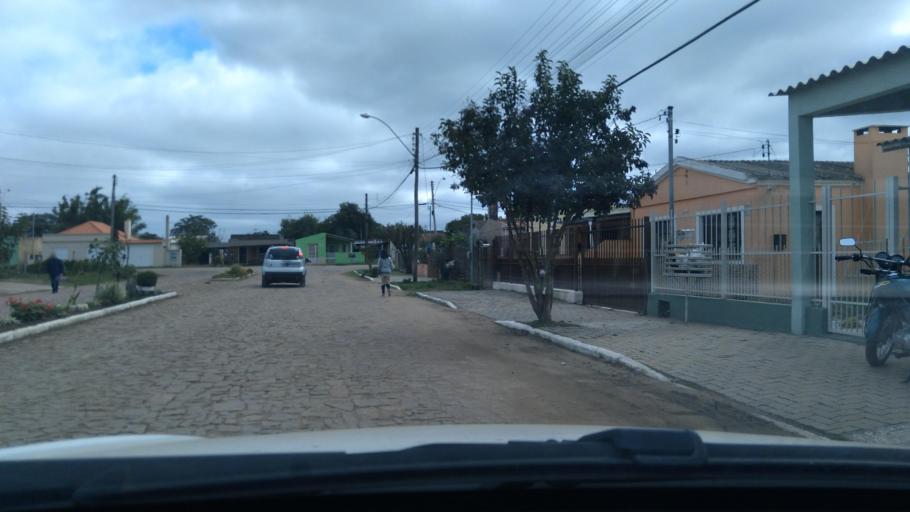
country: BR
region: Rio Grande do Sul
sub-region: Dom Pedrito
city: Dom Pedrito
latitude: -30.9806
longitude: -54.6614
